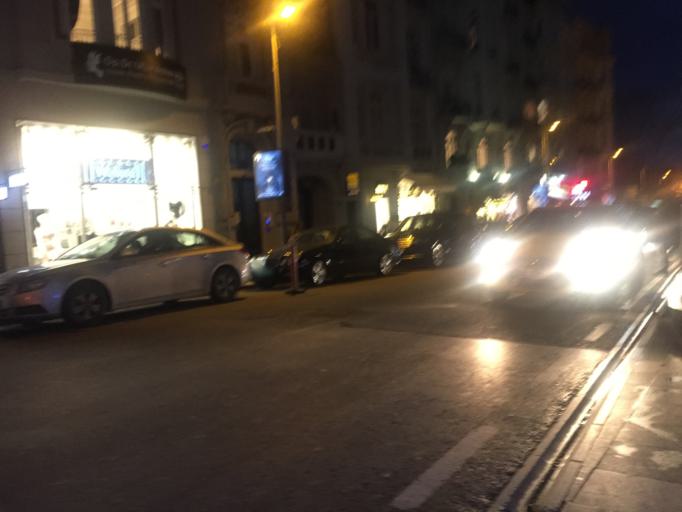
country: TR
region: Istanbul
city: Sisli
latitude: 41.0483
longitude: 28.9946
